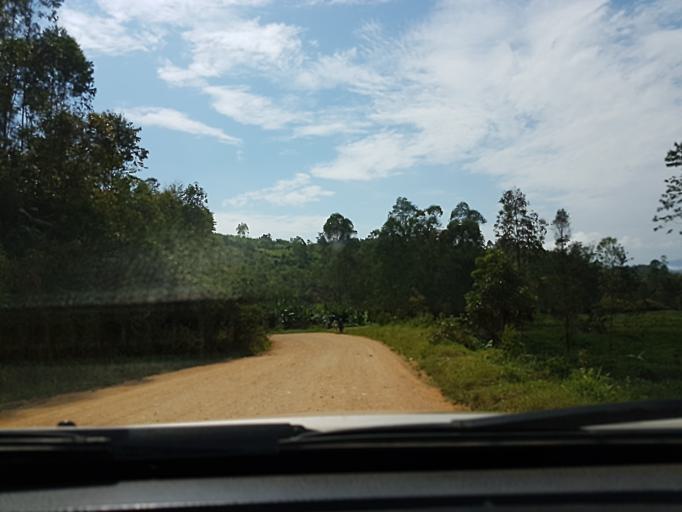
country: CD
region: South Kivu
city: Bukavu
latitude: -2.6341
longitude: 28.8755
